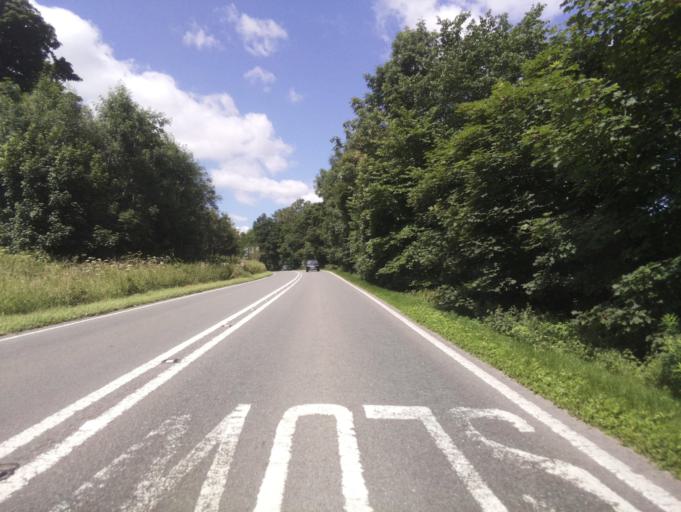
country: GB
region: England
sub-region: Derbyshire
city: Bakewell
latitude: 53.1403
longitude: -1.7544
